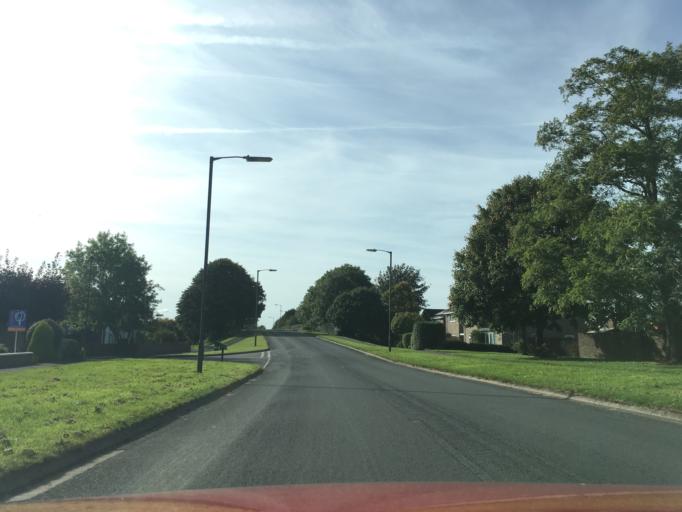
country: GB
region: England
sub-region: South Gloucestershire
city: Yate
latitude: 51.5477
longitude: -2.4072
